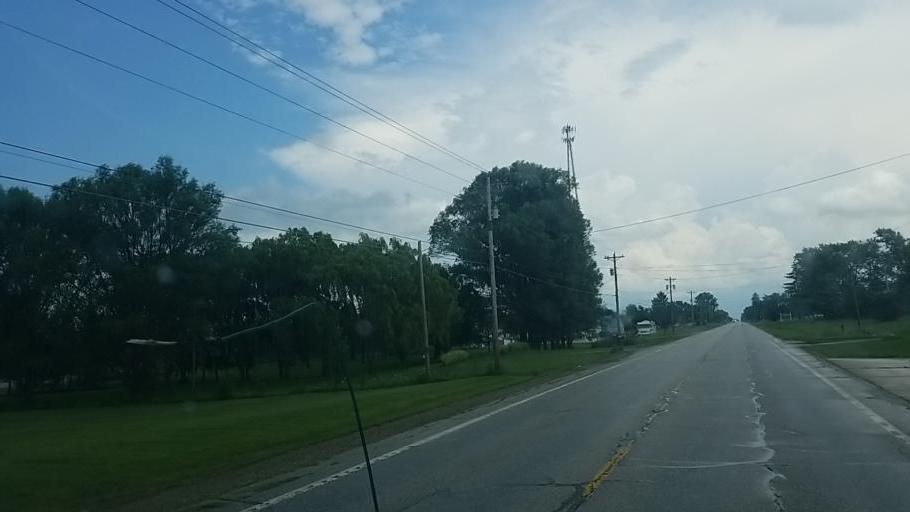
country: US
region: Ohio
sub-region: Lorain County
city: Grafton
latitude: 41.1679
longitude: -82.0075
